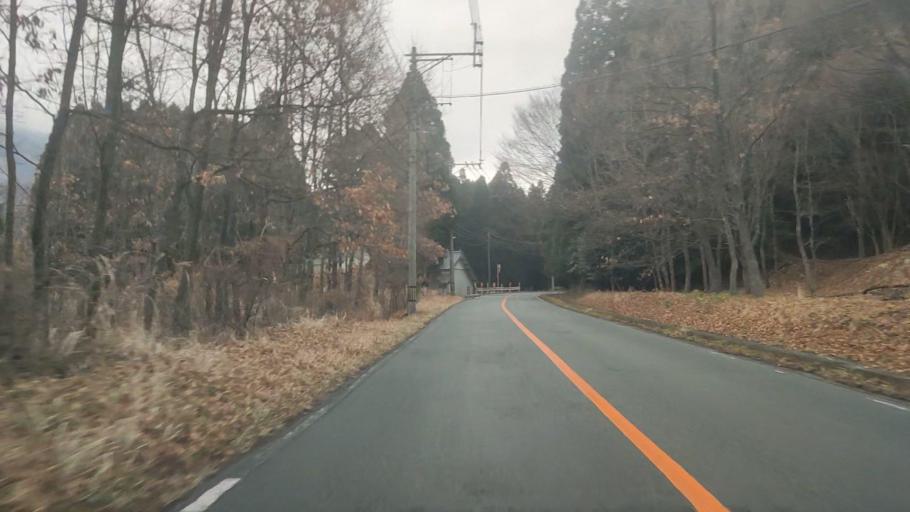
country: JP
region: Kumamoto
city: Aso
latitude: 32.8584
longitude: 131.1618
